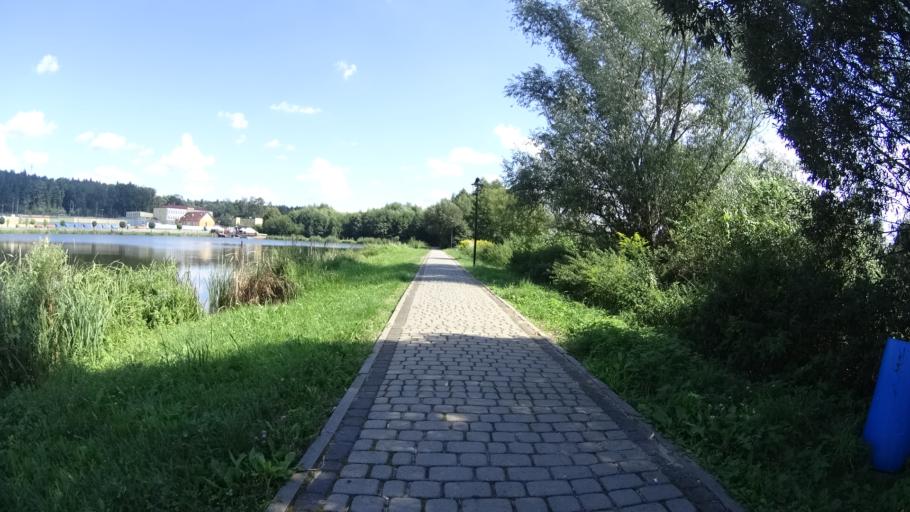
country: PL
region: Masovian Voivodeship
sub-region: Powiat grojecki
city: Mogielnica
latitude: 51.6973
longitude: 20.7224
